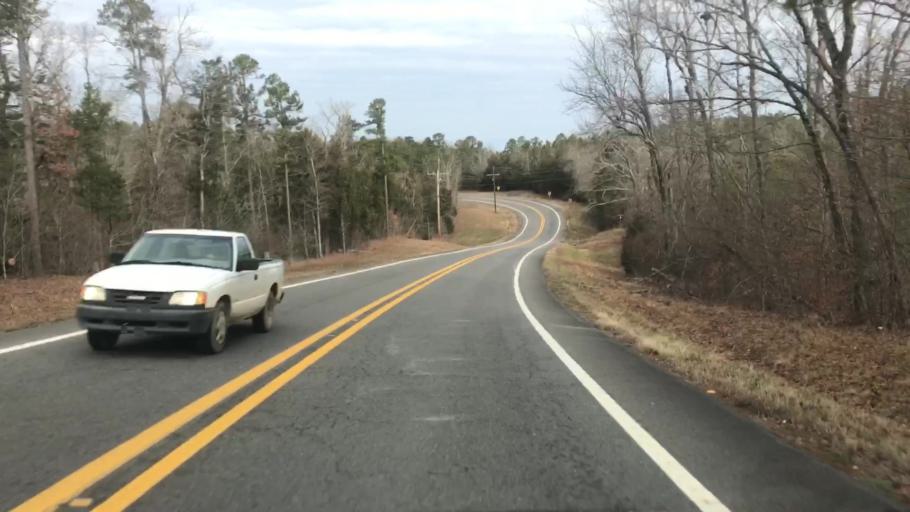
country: US
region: Arkansas
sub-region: Montgomery County
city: Mount Ida
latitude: 34.6170
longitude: -93.7036
